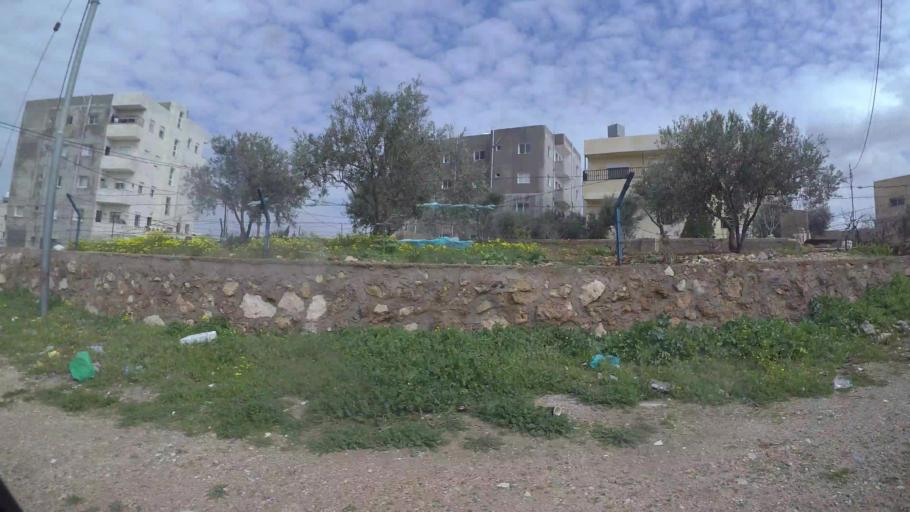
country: JO
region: Amman
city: Al Jubayhah
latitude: 32.0660
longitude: 35.8319
